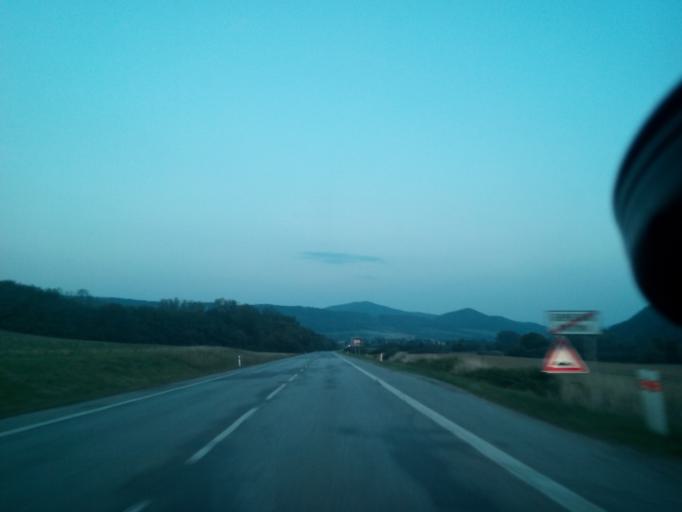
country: SK
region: Kosicky
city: Roznava
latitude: 48.7089
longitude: 20.4859
